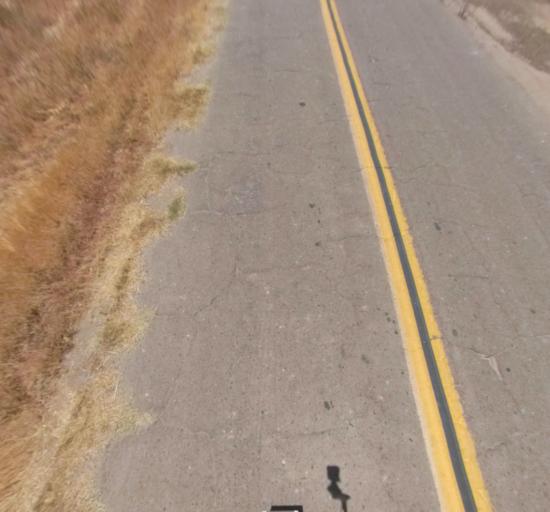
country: US
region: California
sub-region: Madera County
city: Chowchilla
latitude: 37.0619
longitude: -120.2662
